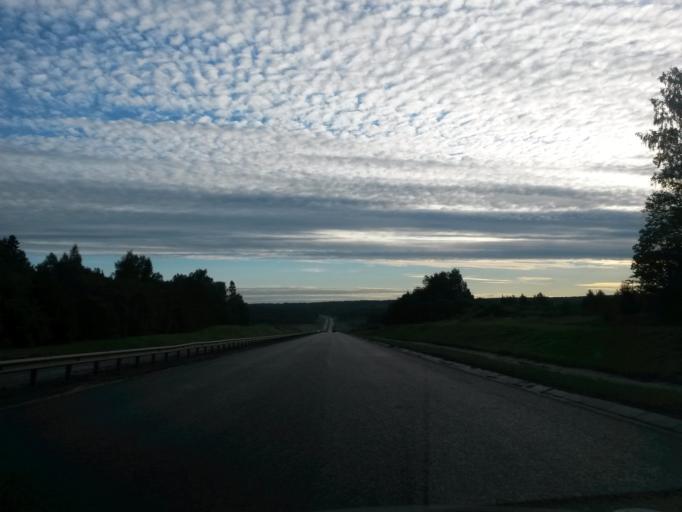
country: RU
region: Vladimir
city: Strunino
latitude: 56.5290
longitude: 38.5728
